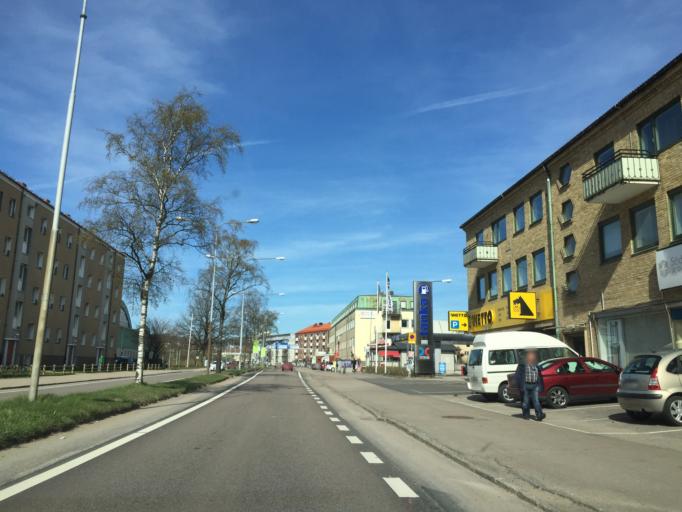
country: SE
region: Vaestra Goetaland
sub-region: Uddevalla Kommun
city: Uddevalla
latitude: 58.3457
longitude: 11.9295
